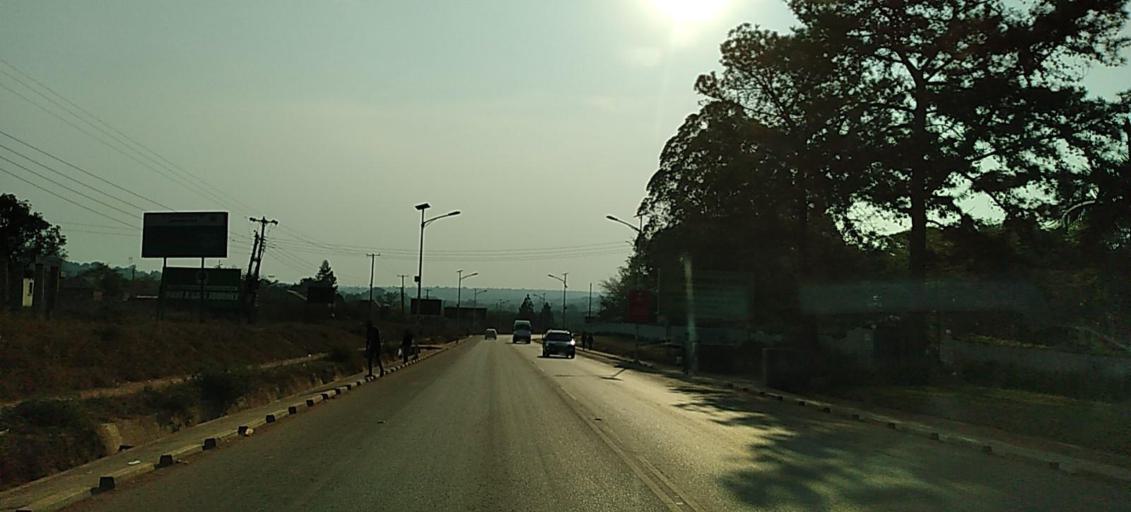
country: ZM
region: North-Western
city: Solwezi
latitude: -12.1887
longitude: 26.4281
